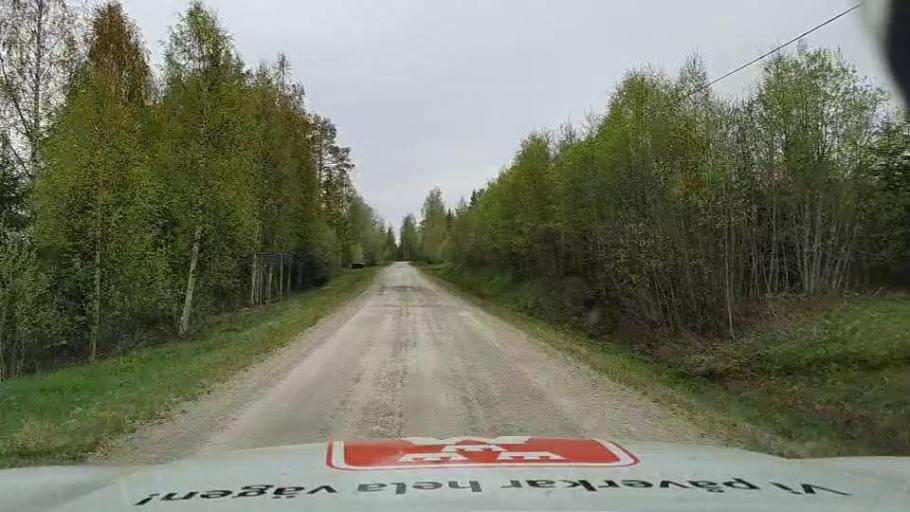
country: SE
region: Jaemtland
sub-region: Bergs Kommun
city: Hoverberg
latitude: 62.6796
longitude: 14.7682
